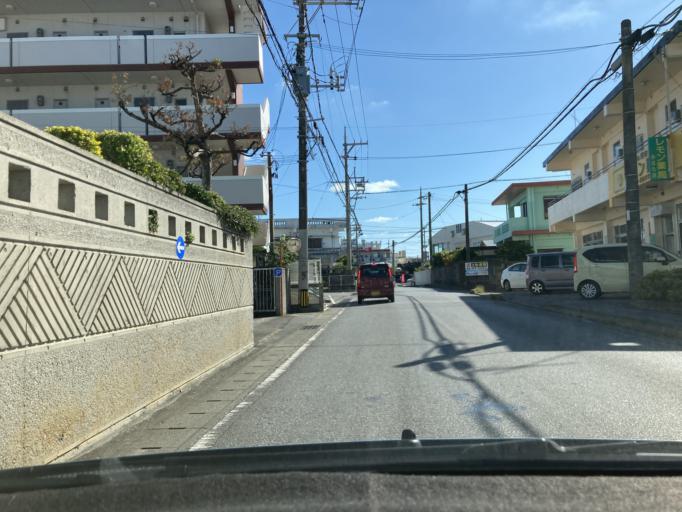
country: JP
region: Okinawa
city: Okinawa
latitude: 26.3507
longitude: 127.8251
